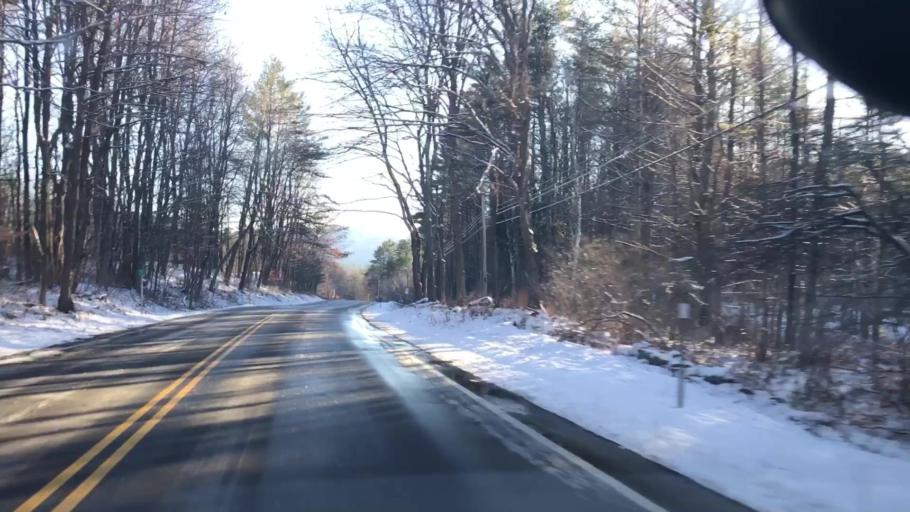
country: US
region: New Hampshire
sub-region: Grafton County
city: Haverhill
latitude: 43.9822
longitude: -72.0808
